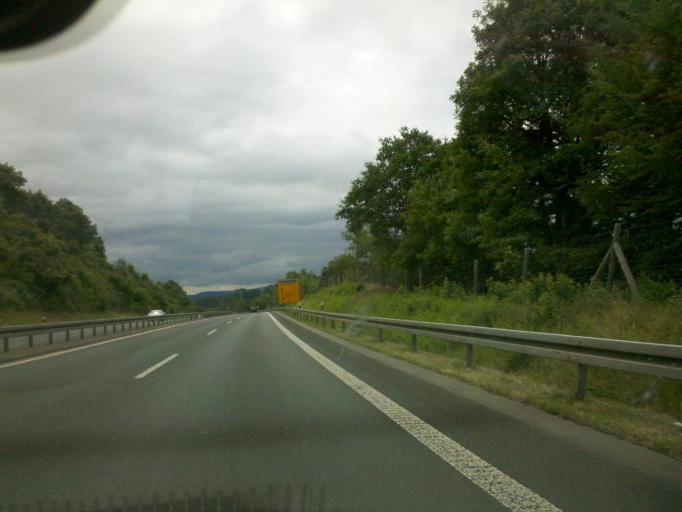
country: DE
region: North Rhine-Westphalia
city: Kreuztal
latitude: 50.9434
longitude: 8.0052
